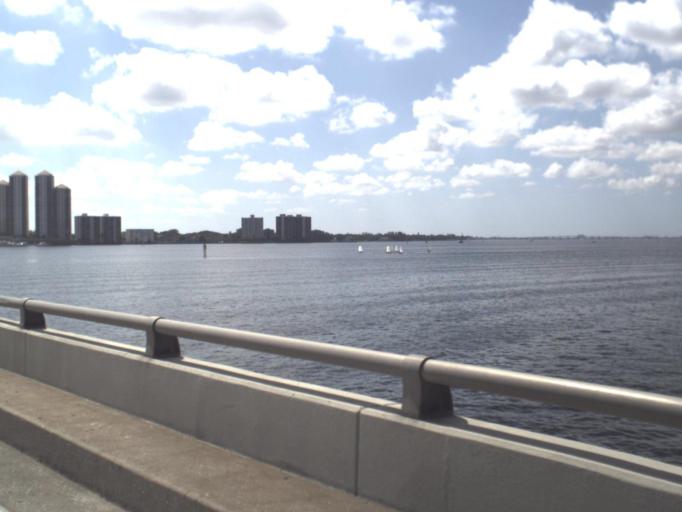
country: US
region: Florida
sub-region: Lee County
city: North Fort Myers
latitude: 26.6543
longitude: -81.8803
